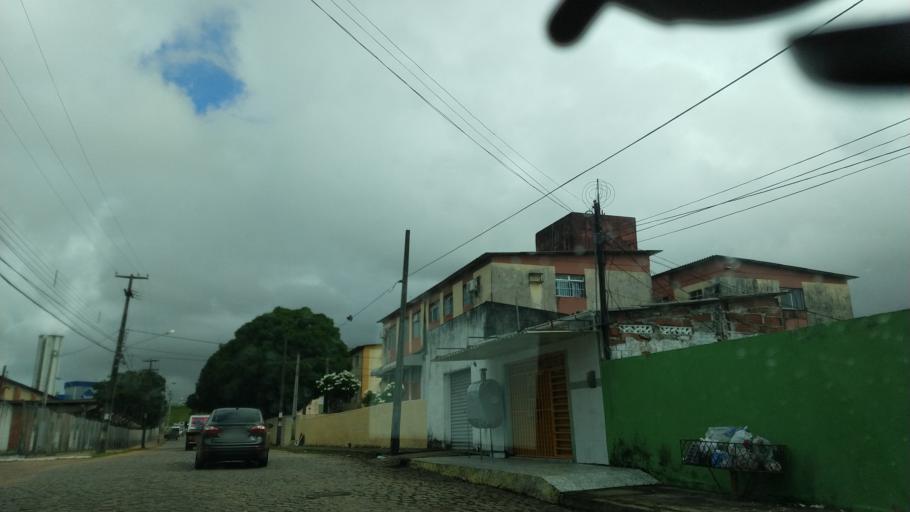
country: BR
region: Rio Grande do Norte
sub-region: Natal
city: Natal
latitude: -5.8597
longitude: -35.2112
